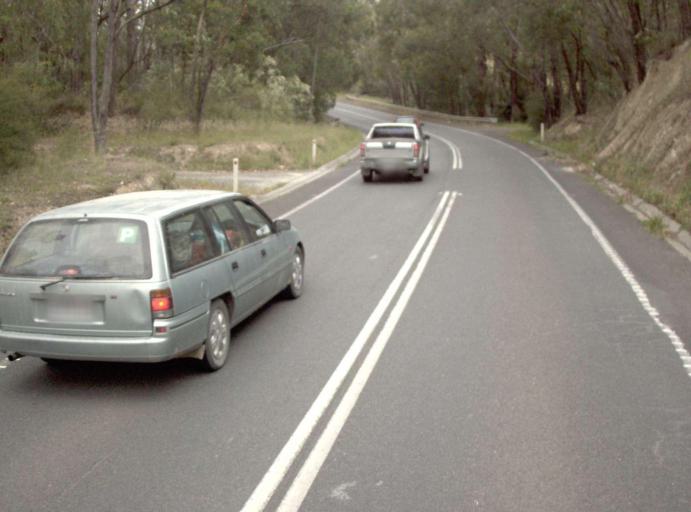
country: AU
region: Victoria
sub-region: Yarra Ranges
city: Yarra Glen
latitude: -37.5634
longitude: 145.4159
